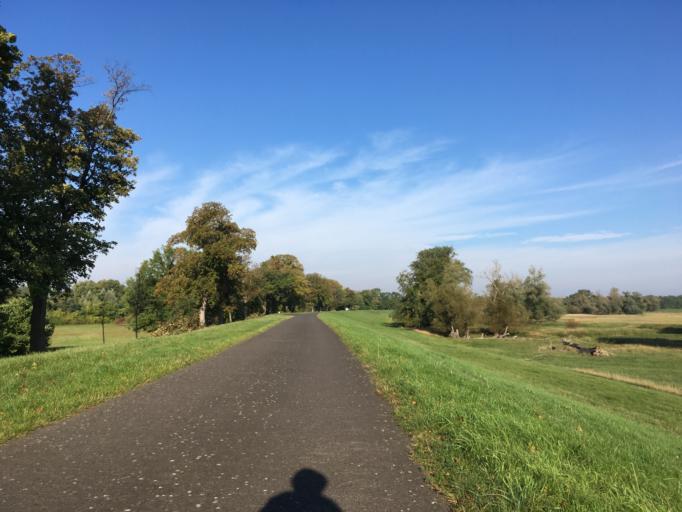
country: DE
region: Brandenburg
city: Reitwein
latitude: 52.5105
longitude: 14.6024
